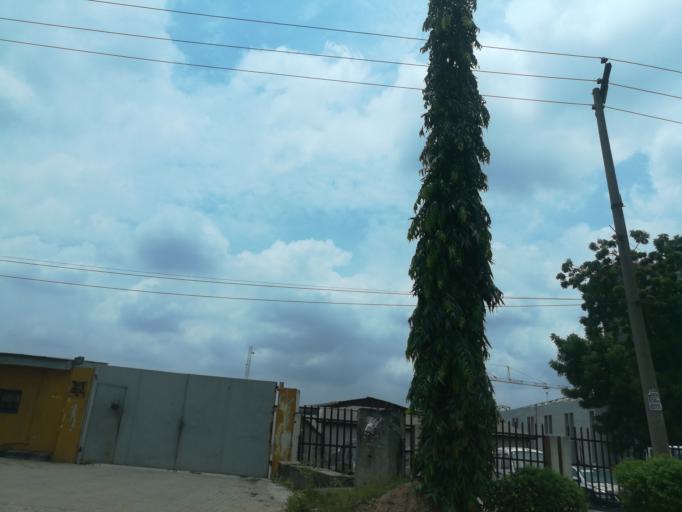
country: NG
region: Lagos
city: Ojota
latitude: 6.5944
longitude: 3.3707
